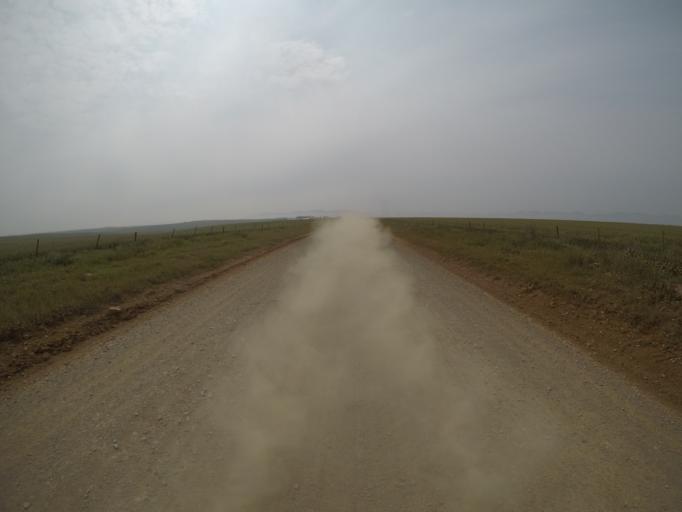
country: ZA
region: Western Cape
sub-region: City of Cape Town
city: Kraaifontein
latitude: -33.7171
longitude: 18.6808
